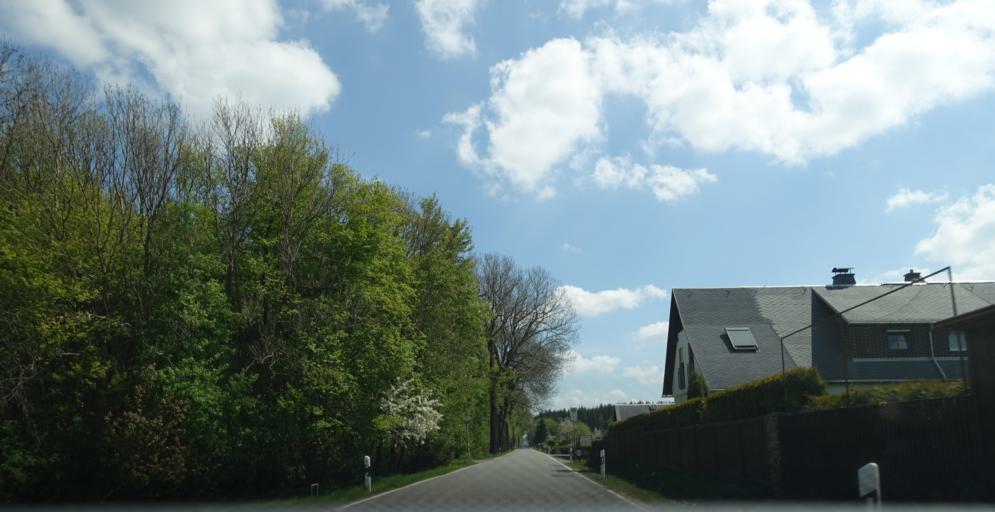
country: DE
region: Saxony
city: Grosshartmannsdorf
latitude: 50.8024
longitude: 13.3373
